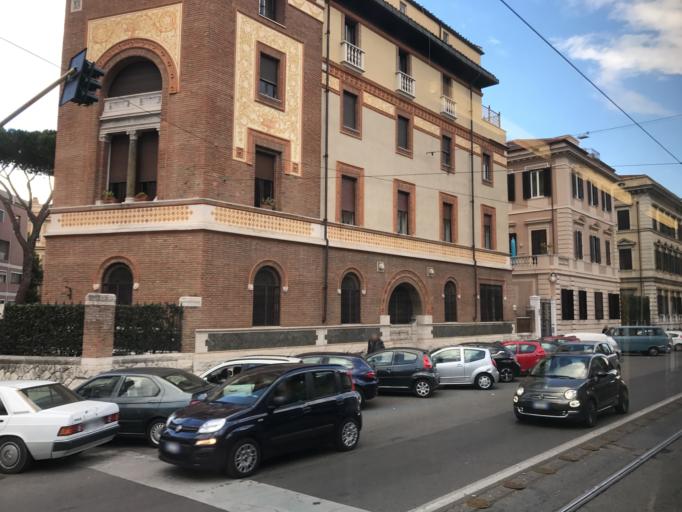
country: IT
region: Latium
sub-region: Citta metropolitana di Roma Capitale
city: Rome
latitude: 41.9122
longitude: 12.5076
